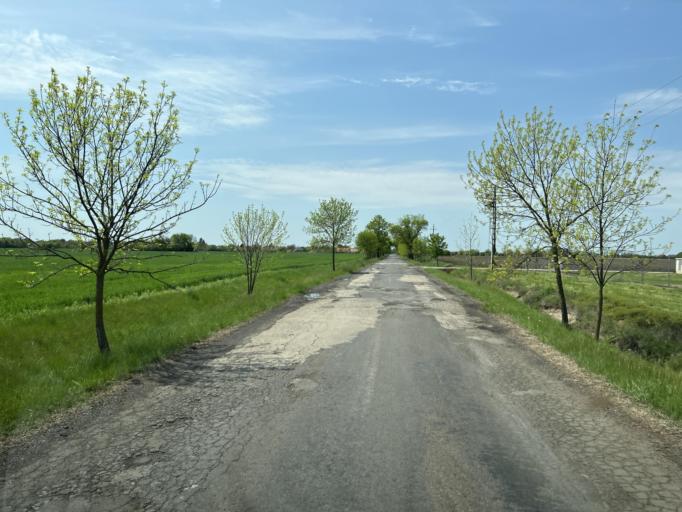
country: HU
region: Pest
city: Tapiogyorgye
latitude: 47.3482
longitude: 19.9520
